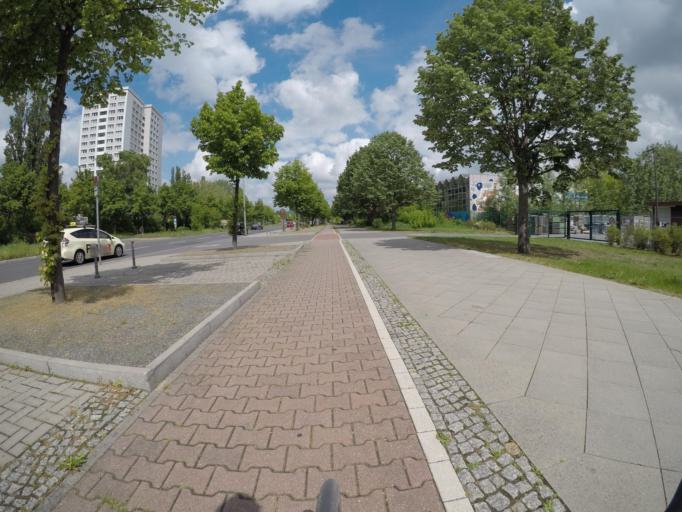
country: DE
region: Berlin
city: Marzahn
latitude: 52.5392
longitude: 13.5696
